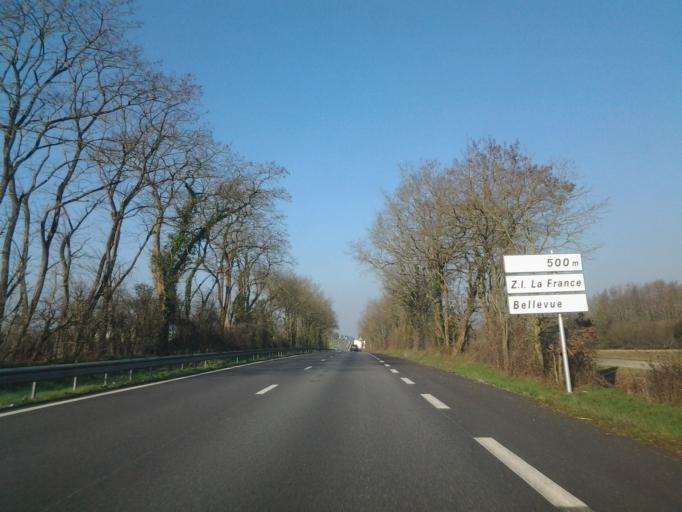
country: FR
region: Pays de la Loire
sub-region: Departement de la Vendee
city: La Genetouze
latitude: 46.7117
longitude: -1.5276
